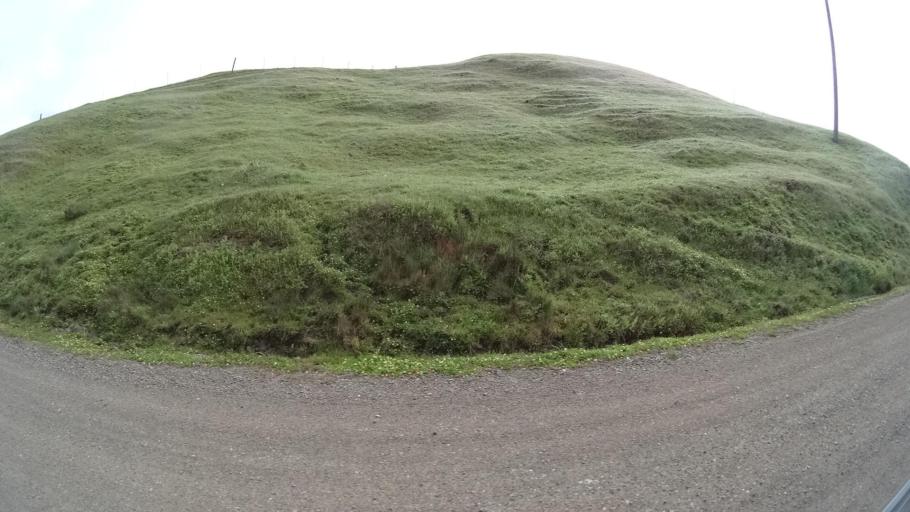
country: US
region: California
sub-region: Humboldt County
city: Redway
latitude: 40.2022
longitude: -123.7131
